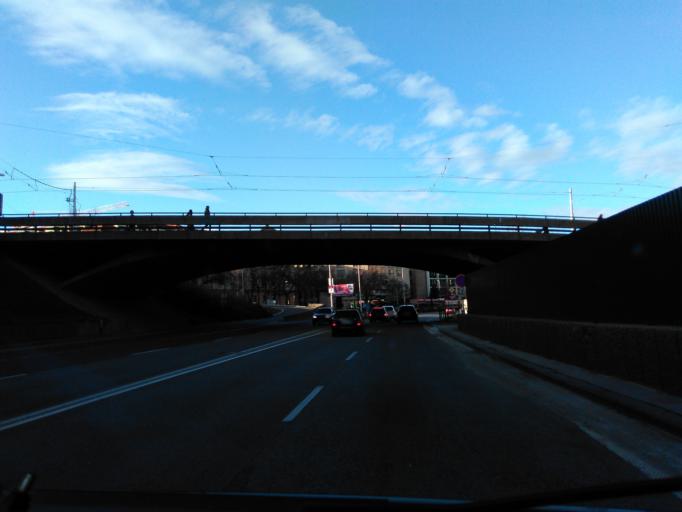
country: SK
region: Bratislavsky
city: Bratislava
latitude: 48.1442
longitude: 17.1039
